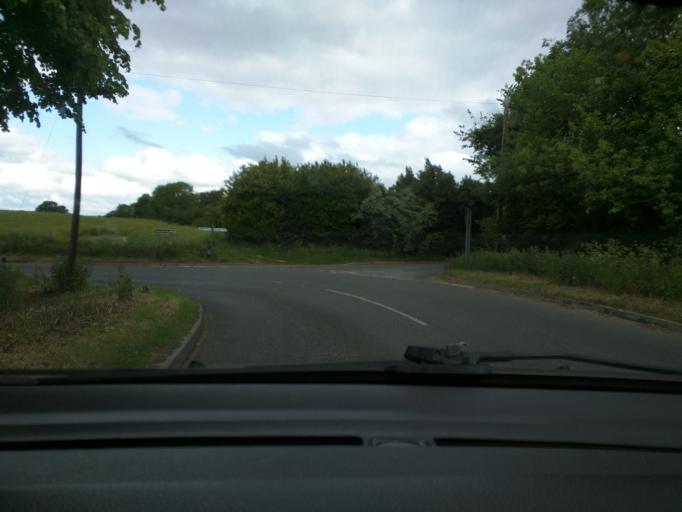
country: GB
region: England
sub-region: Suffolk
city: Leiston
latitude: 52.2127
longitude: 1.5510
